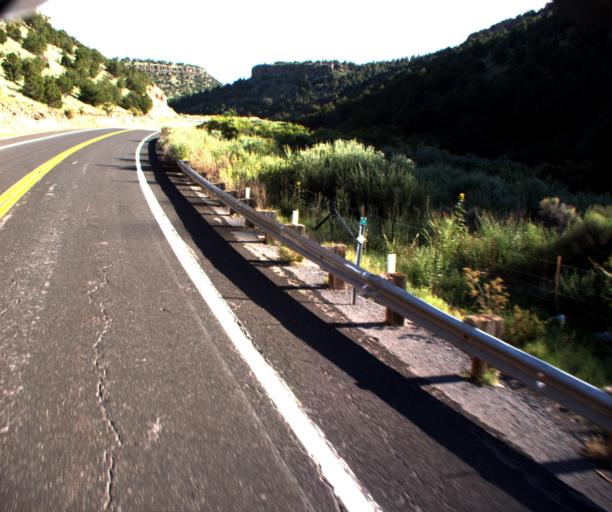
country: US
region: Arizona
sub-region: Apache County
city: Eagar
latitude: 34.0857
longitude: -109.2031
